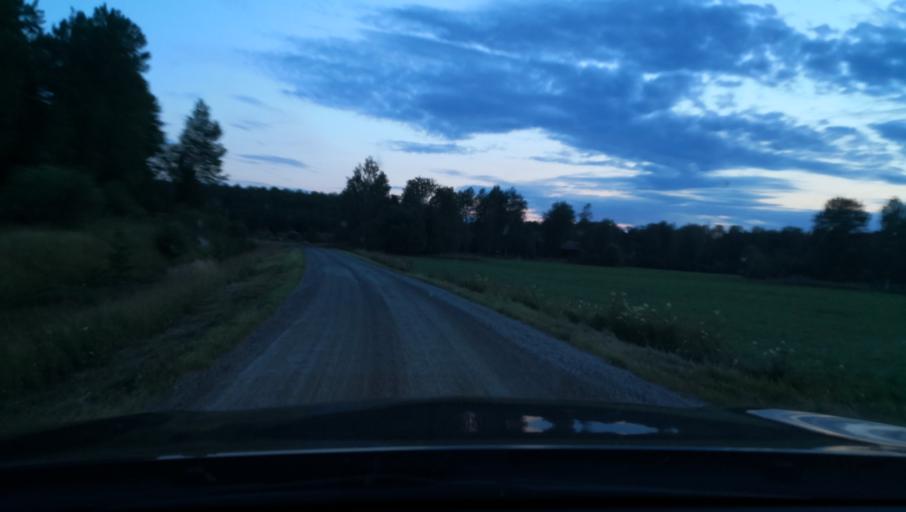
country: SE
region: Uppsala
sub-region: Heby Kommun
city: OEstervala
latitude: 60.0151
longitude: 17.3002
